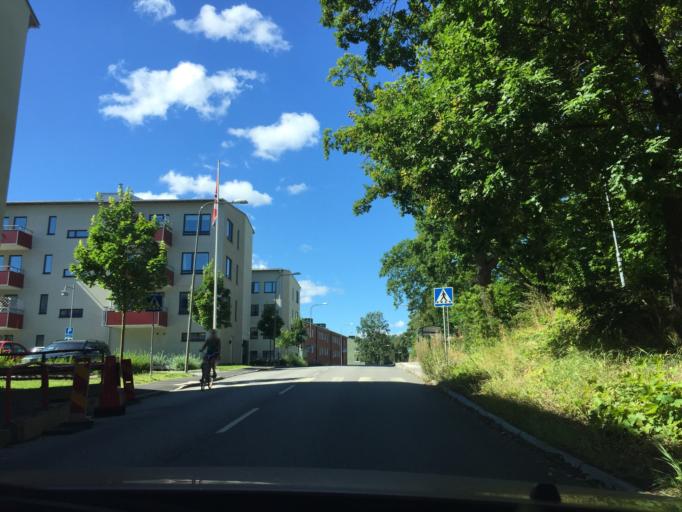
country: SE
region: Stockholm
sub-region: Nacka Kommun
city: Nacka
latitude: 59.3026
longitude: 18.1279
